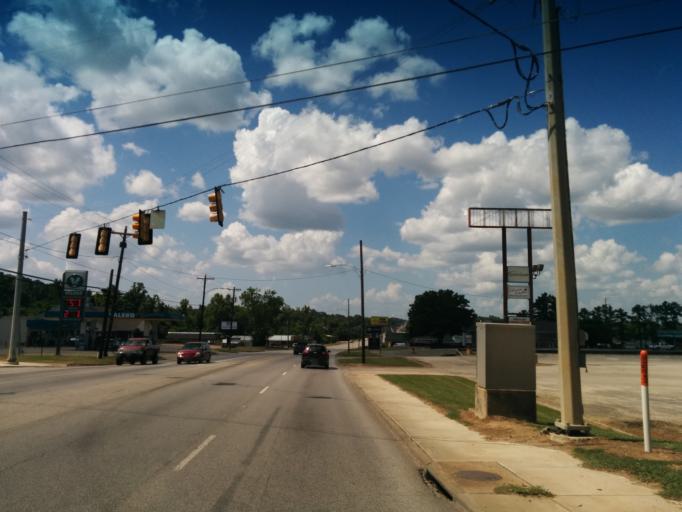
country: US
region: Texas
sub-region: Jasper County
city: Jasper
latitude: 30.9141
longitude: -93.9964
